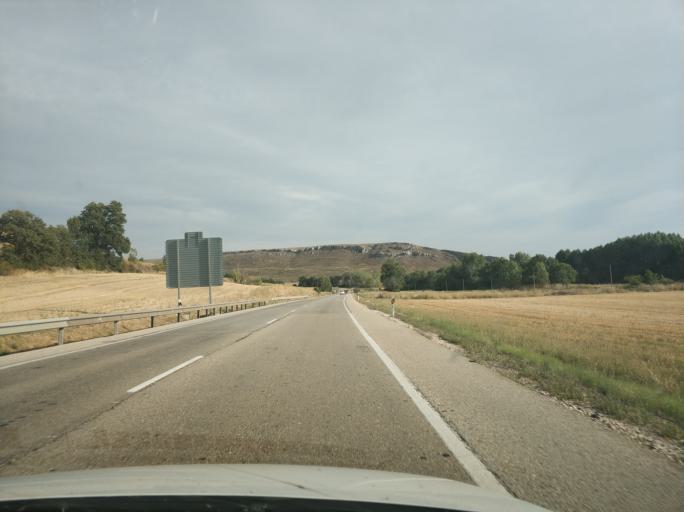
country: ES
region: Castille and Leon
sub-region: Provincia de Burgos
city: Quintanaortuno
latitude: 42.5007
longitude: -3.6999
